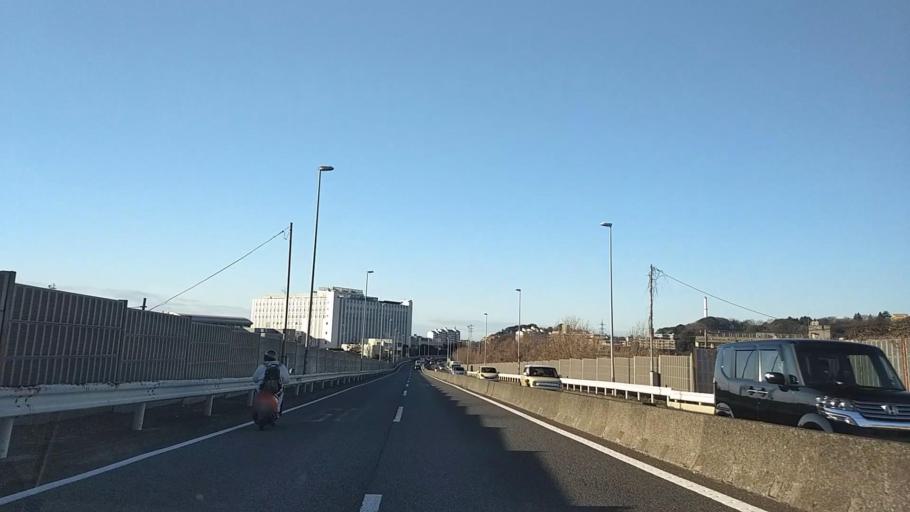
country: JP
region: Kanagawa
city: Fujisawa
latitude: 35.3543
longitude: 139.4859
